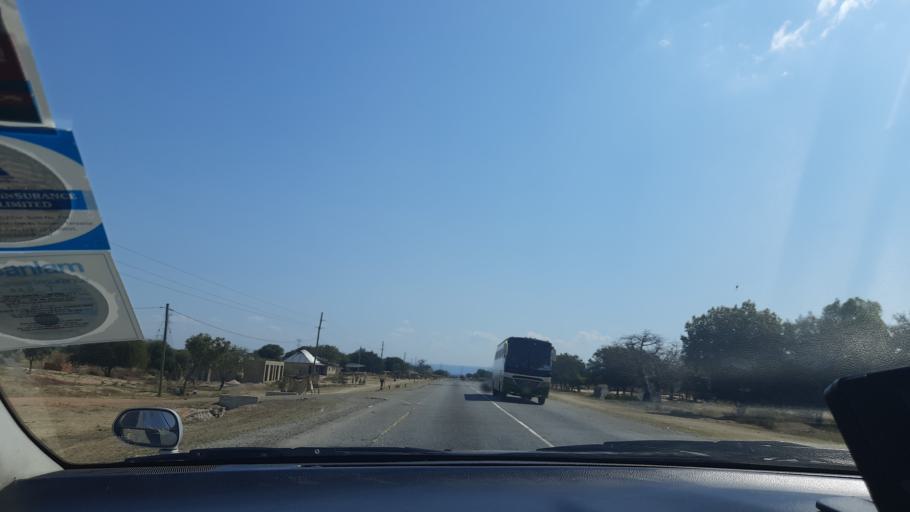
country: TZ
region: Singida
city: Kintinku
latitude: -5.8800
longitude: 35.1271
